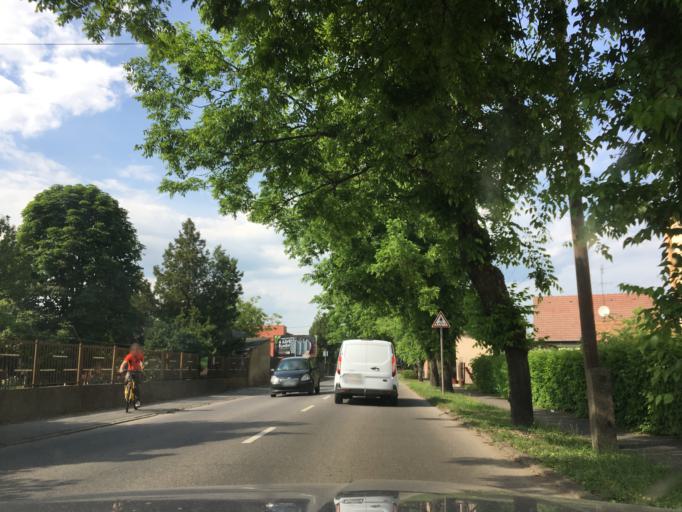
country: HU
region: Hajdu-Bihar
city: Debrecen
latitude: 47.5218
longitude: 21.6592
